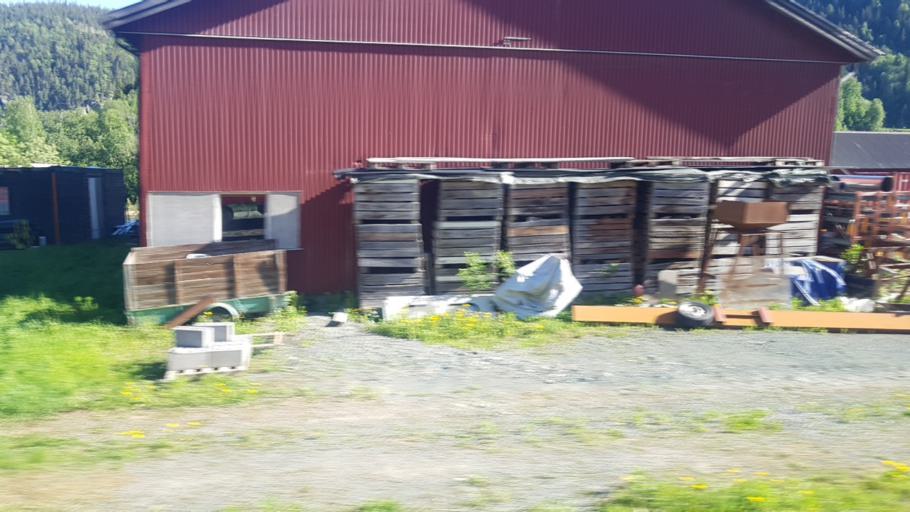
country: NO
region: Sor-Trondelag
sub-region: Midtre Gauldal
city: Storen
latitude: 63.0874
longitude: 10.2488
